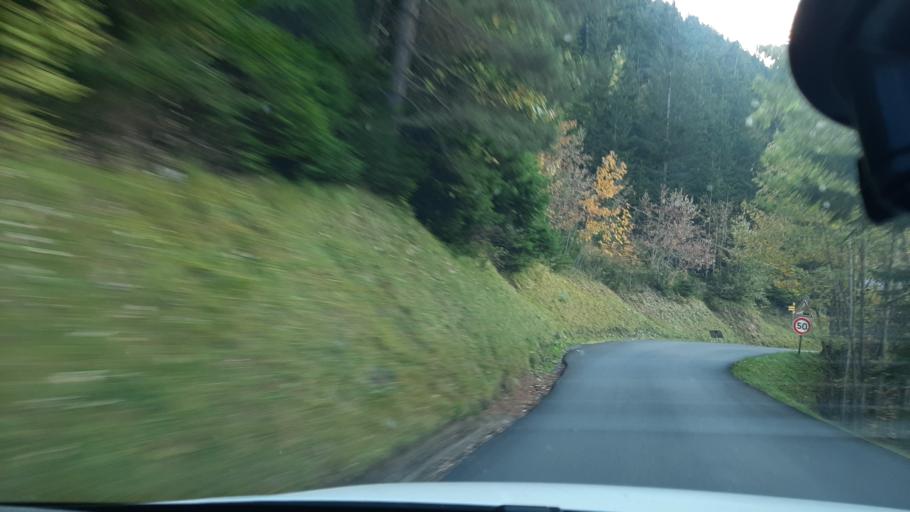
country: FR
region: Rhone-Alpes
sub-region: Departement de la Savoie
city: Saint-Jean-de-Maurienne
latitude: 45.1972
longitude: 6.3045
